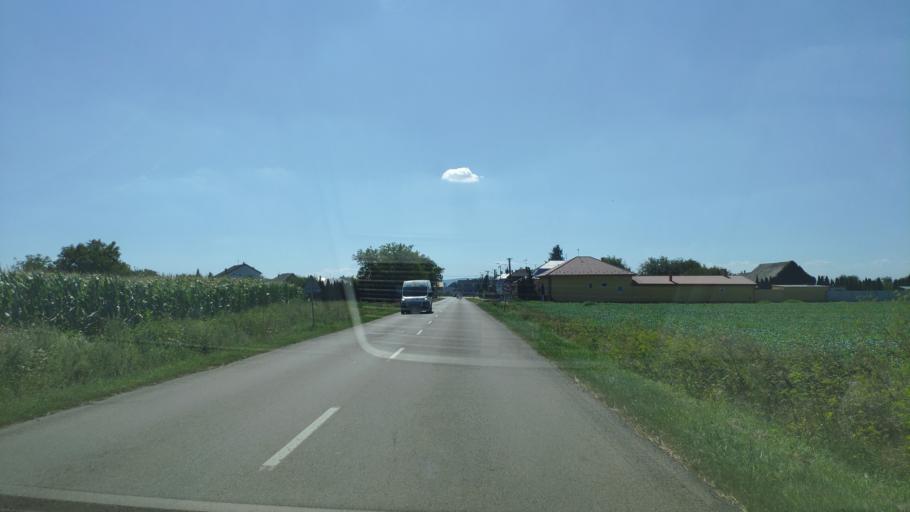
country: SK
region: Kosicky
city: Trebisov
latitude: 48.5459
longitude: 21.8876
